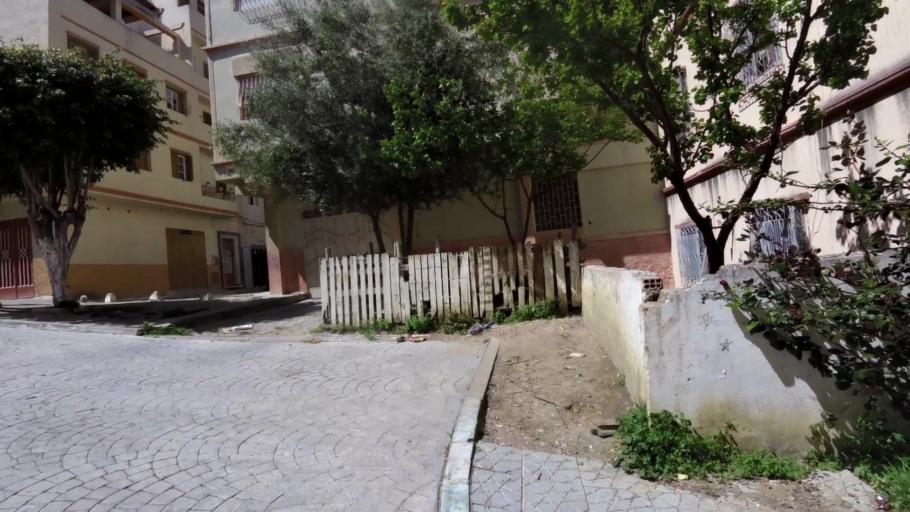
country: MA
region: Tanger-Tetouan
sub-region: Tanger-Assilah
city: Tangier
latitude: 35.7515
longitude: -5.8152
